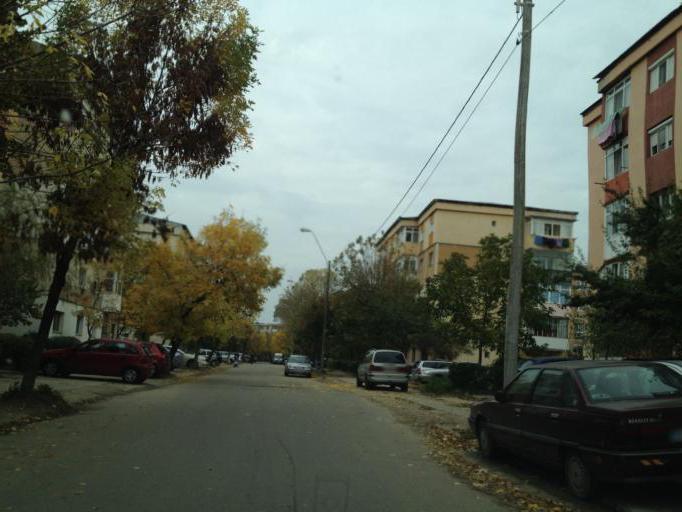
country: RO
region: Dolj
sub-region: Municipiul Craiova
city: Popoveni
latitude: 44.2968
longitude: 23.7944
